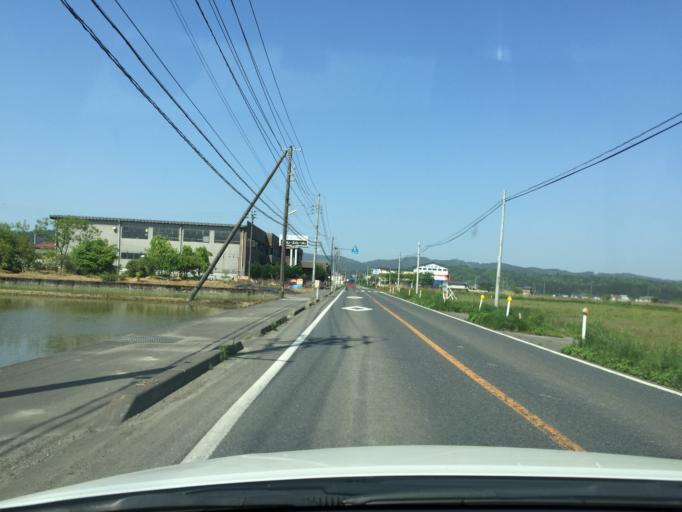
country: JP
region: Niigata
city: Muramatsu
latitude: 37.6876
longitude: 139.1582
